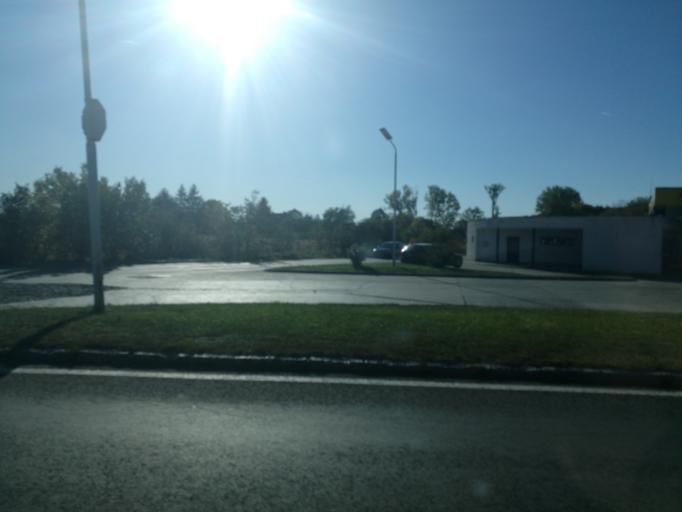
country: RO
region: Brasov
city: Brasov
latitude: 45.6789
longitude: 25.5868
